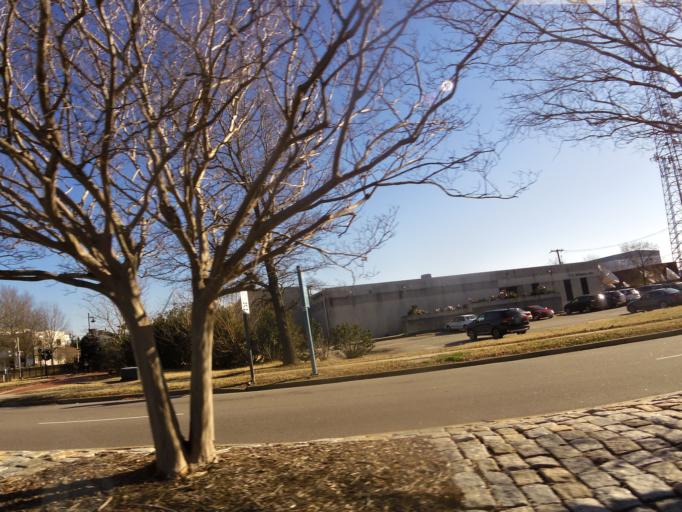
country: US
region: Virginia
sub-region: City of Portsmouth
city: Portsmouth
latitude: 36.8301
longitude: -76.3007
